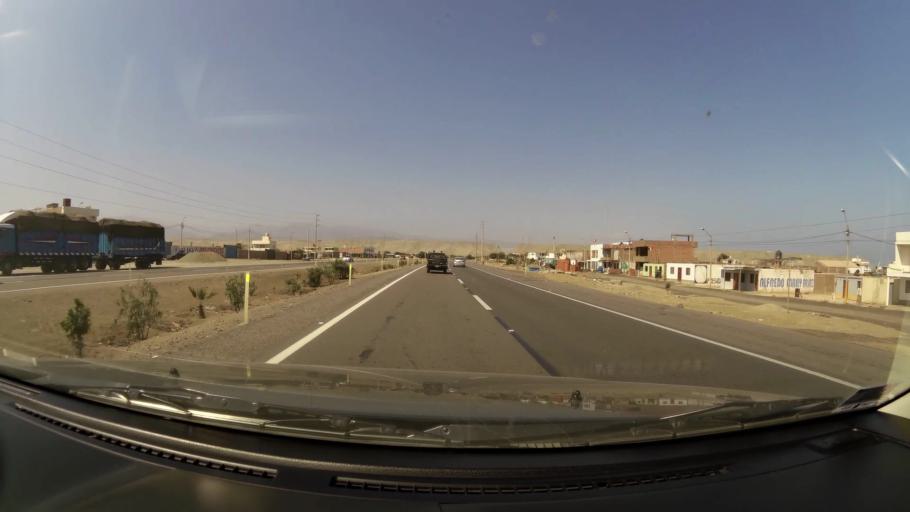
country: PE
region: Lima
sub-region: Provincia de Canete
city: Asia
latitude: -12.7929
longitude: -76.5604
